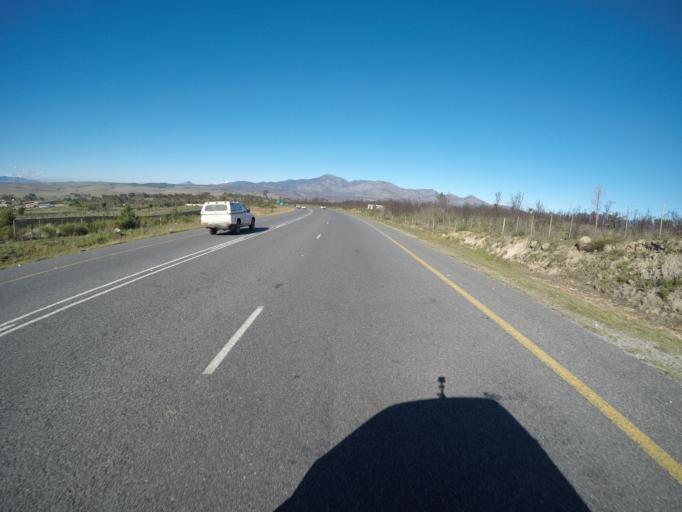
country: ZA
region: Western Cape
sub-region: Overberg District Municipality
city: Hermanus
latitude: -34.2329
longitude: 19.1891
